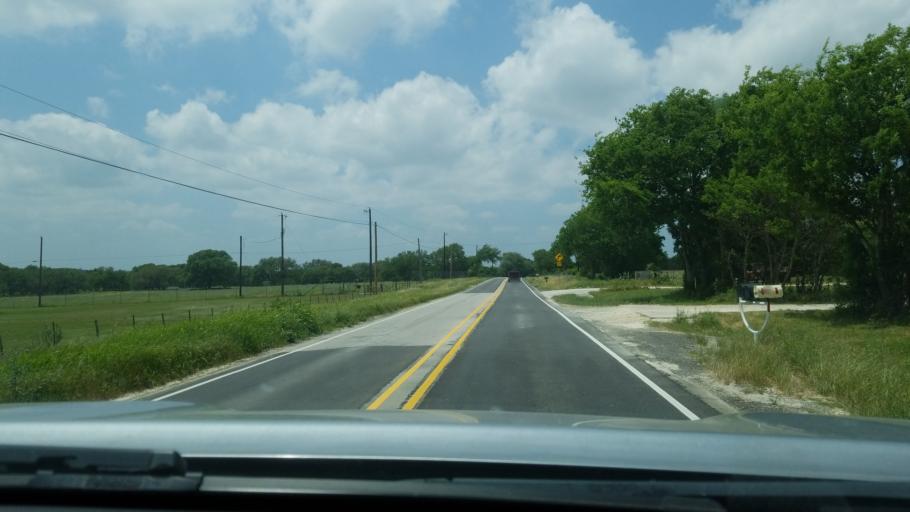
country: US
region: Texas
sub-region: Hays County
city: Dripping Springs
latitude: 30.1492
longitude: -98.0554
